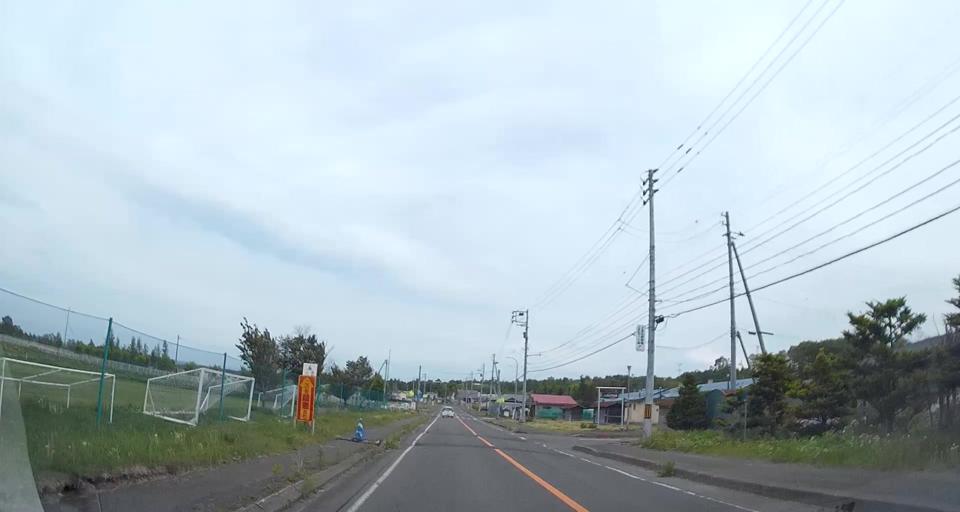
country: JP
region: Hokkaido
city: Chitose
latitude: 42.7698
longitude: 141.8261
